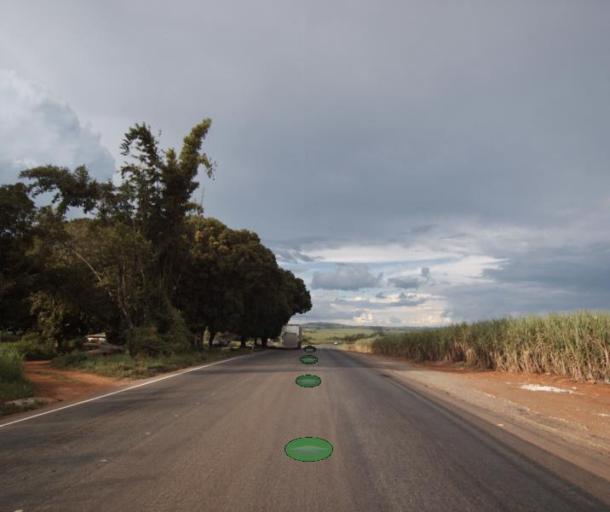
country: BR
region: Goias
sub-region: Ceres
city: Ceres
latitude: -15.1447
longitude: -49.5307
